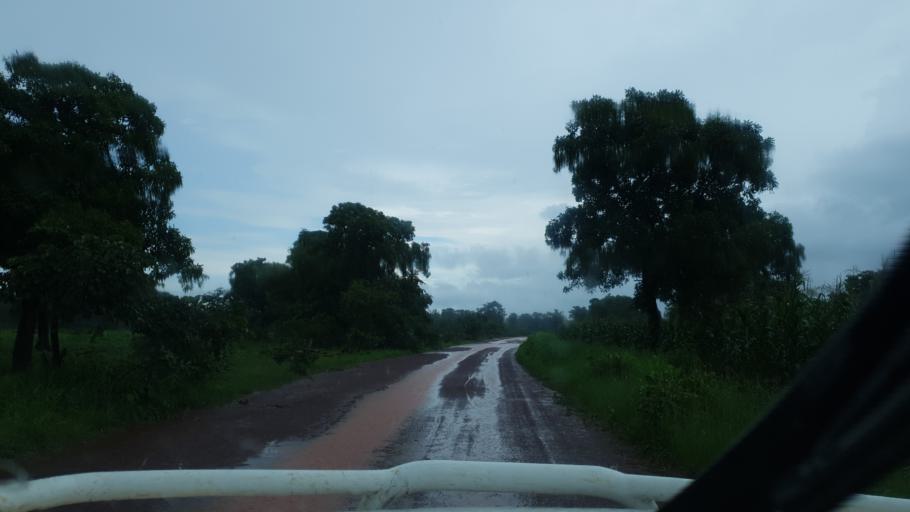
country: ML
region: Sikasso
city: Kolondieba
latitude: 11.5975
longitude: -6.6660
